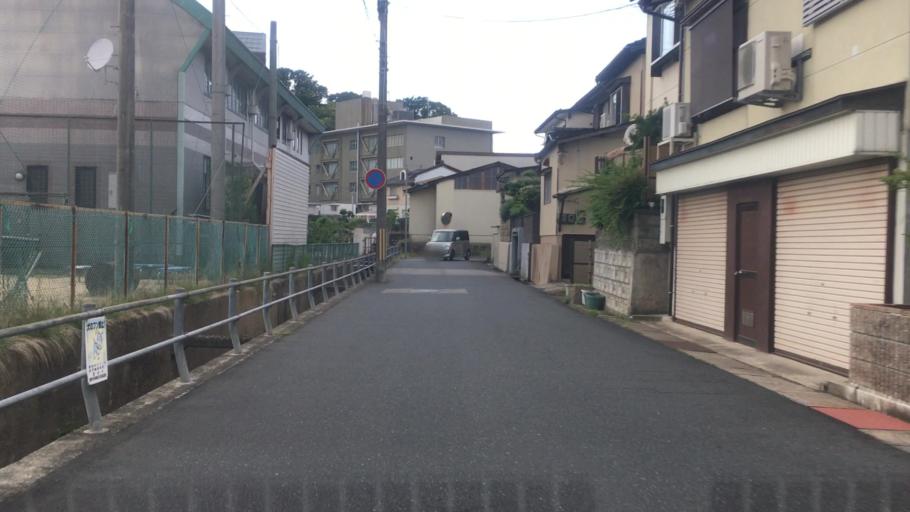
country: JP
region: Hyogo
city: Toyooka
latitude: 35.5383
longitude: 134.8228
